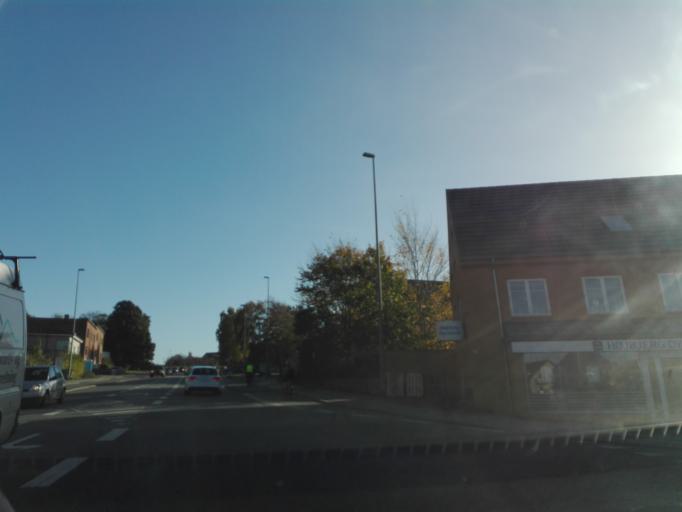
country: DK
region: Central Jutland
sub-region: Arhus Kommune
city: Arhus
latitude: 56.1150
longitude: 10.2073
